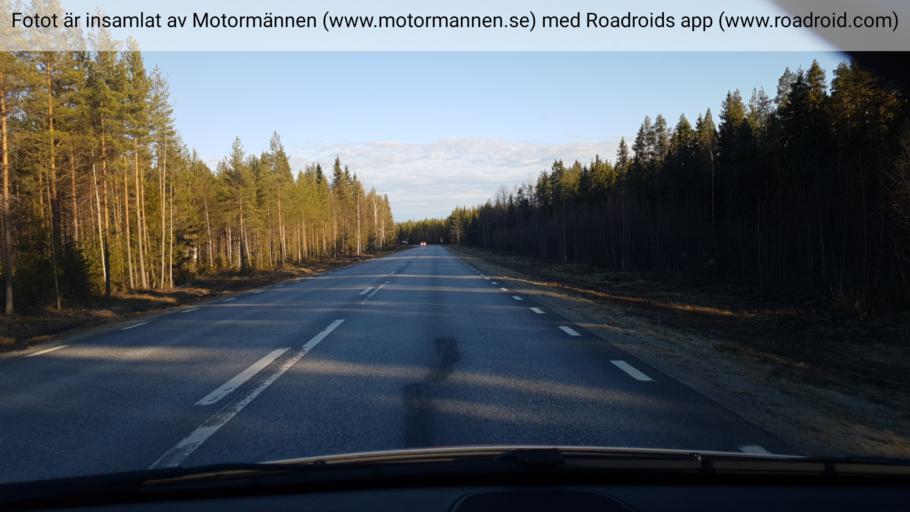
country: SE
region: Vaesterbotten
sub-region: Vannas Kommun
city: Vaennaes
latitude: 63.9284
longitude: 19.7846
